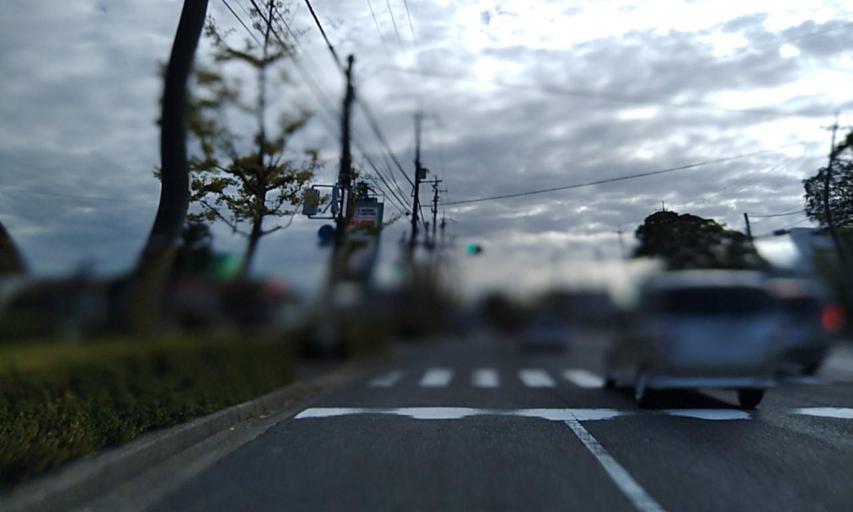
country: JP
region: Wakayama
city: Wakayama-shi
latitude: 34.2540
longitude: 135.1388
